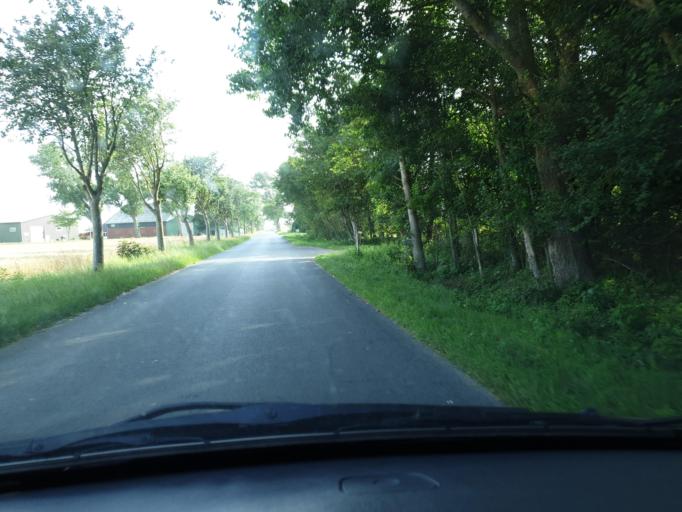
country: DE
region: Schleswig-Holstein
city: Friedrichskoog
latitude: 54.0143
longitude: 8.8644
